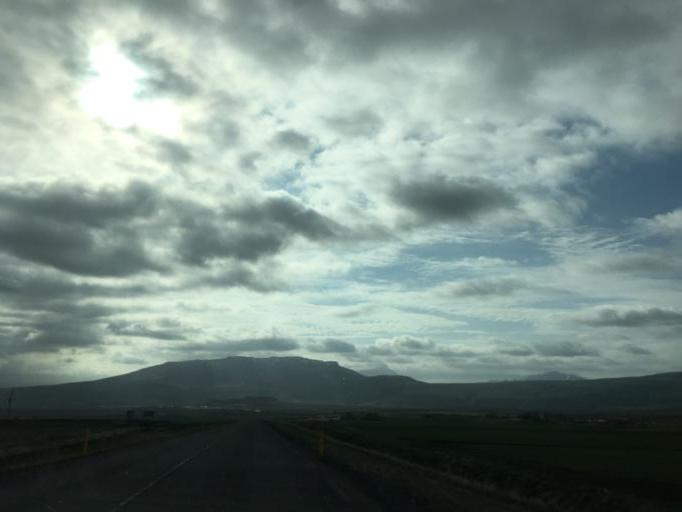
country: IS
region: South
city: Vestmannaeyjar
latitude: 64.3079
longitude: -20.2088
